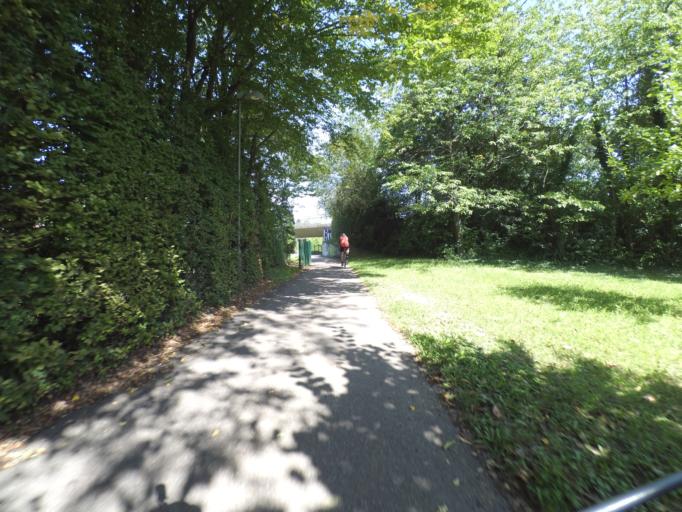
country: DE
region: Baden-Wuerttemberg
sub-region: Freiburg Region
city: Gundelfingen
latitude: 48.0379
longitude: 7.8716
